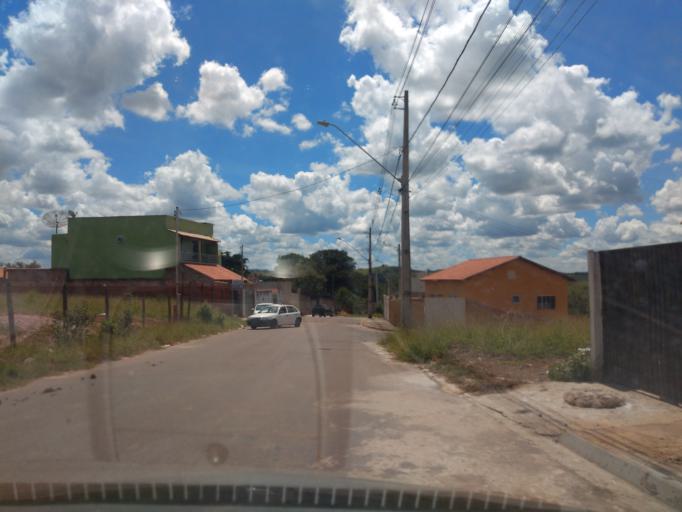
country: BR
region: Minas Gerais
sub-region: Tres Coracoes
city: Tres Coracoes
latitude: -21.6831
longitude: -45.2405
